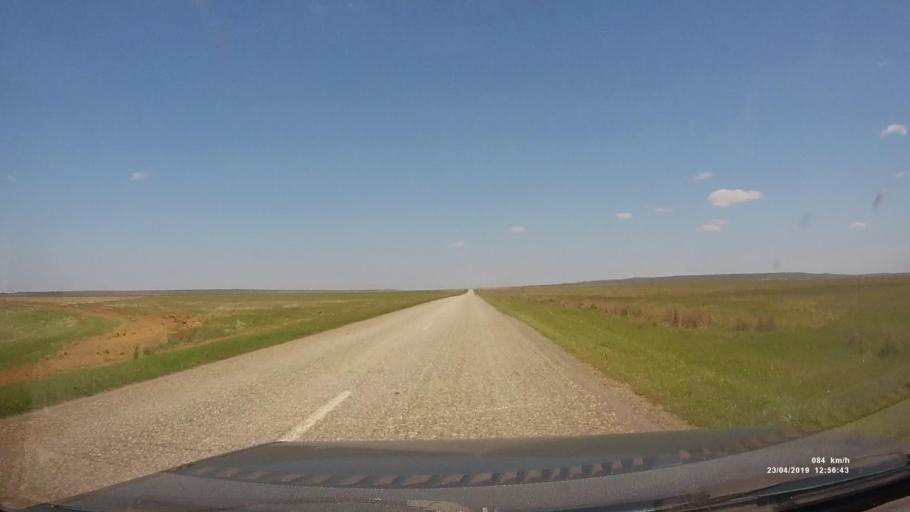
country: RU
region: Kalmykiya
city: Yashalta
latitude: 46.5968
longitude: 42.5743
